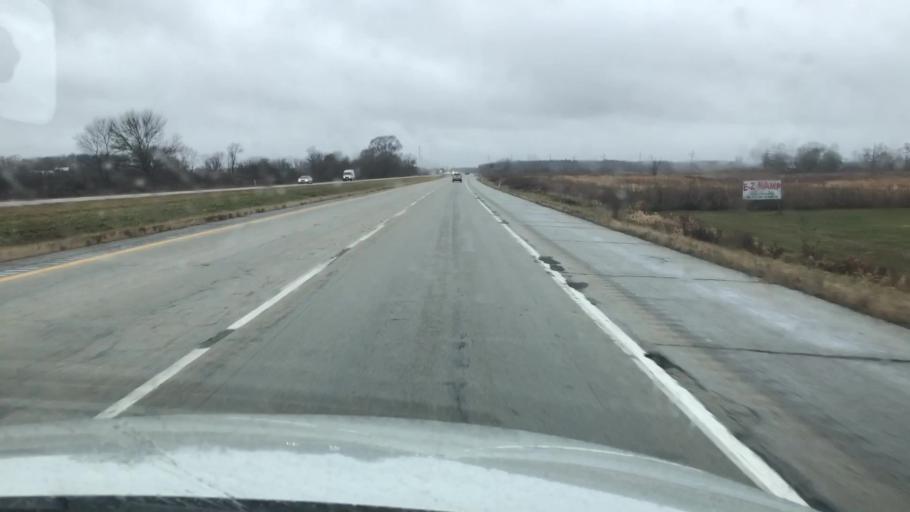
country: US
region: Indiana
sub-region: Starke County
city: Koontz Lake
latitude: 41.3734
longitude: -86.5191
